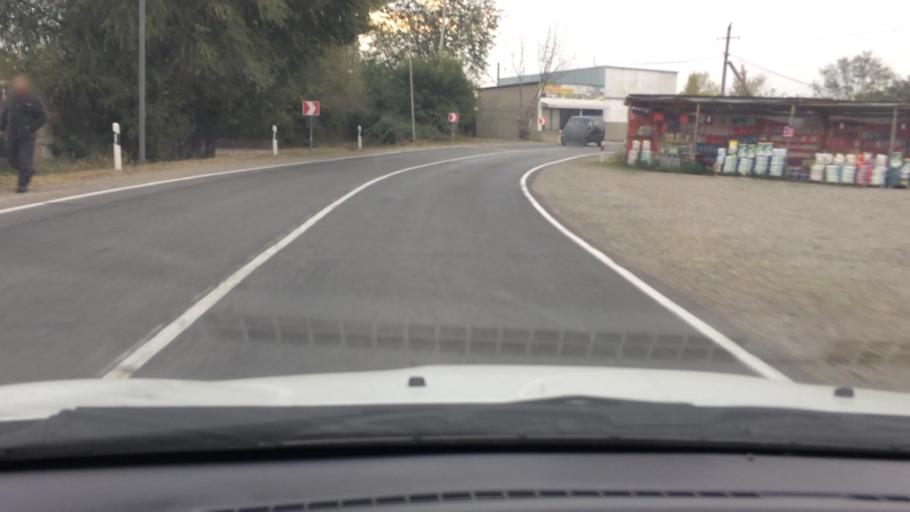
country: GE
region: Kvemo Kartli
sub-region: Marneuli
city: Marneuli
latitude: 41.4644
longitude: 44.8077
